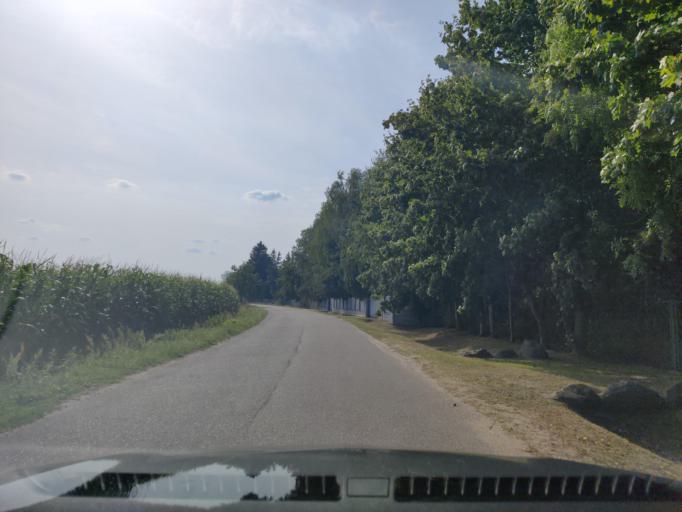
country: PL
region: Masovian Voivodeship
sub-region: Powiat pultuski
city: Obryte
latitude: 52.7716
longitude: 21.2582
